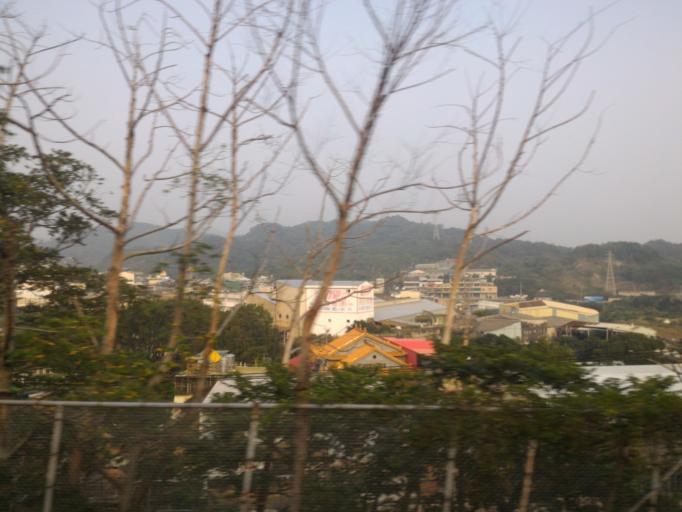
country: TW
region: Taiwan
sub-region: Taoyuan
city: Taoyuan
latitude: 24.9611
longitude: 121.3388
